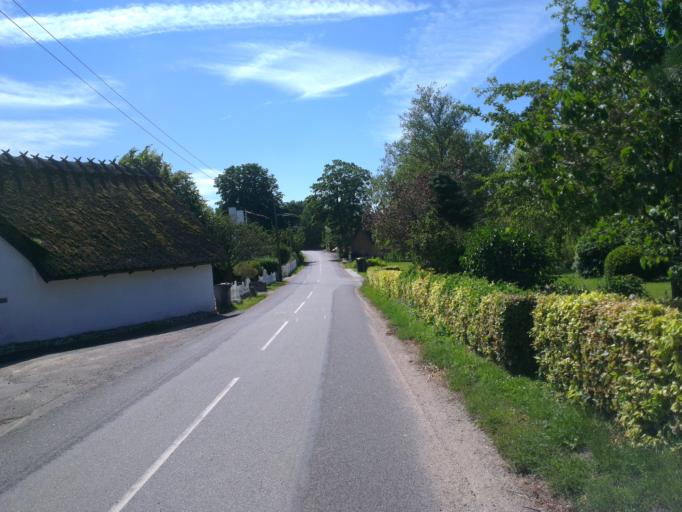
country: DK
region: Capital Region
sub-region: Frederikssund Kommune
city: Slangerup
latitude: 55.8534
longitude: 12.1356
